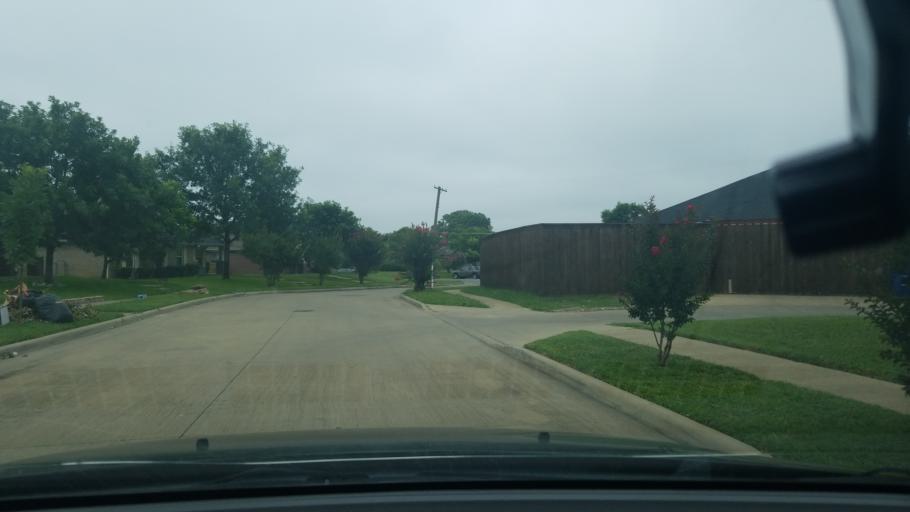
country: US
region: Texas
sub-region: Dallas County
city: Balch Springs
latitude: 32.7559
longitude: -96.6878
